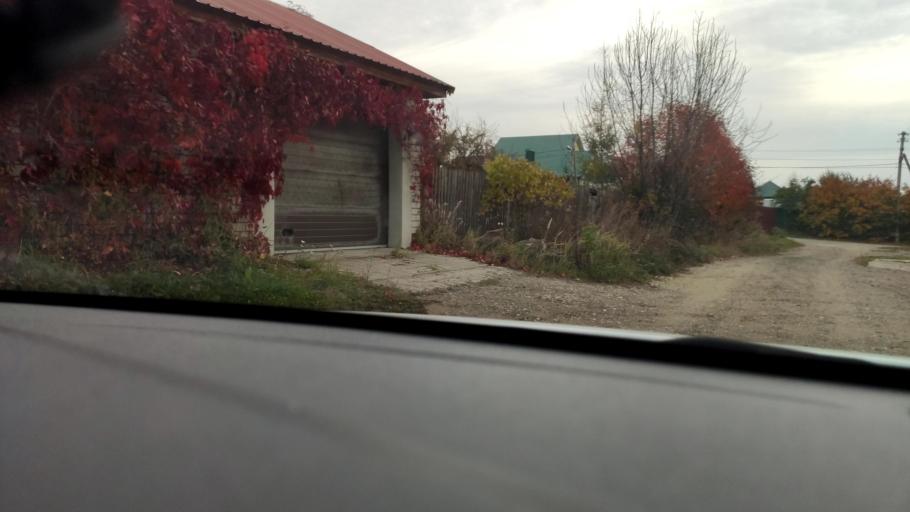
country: RU
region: Tatarstan
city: Stolbishchi
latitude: 55.7668
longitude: 49.2679
